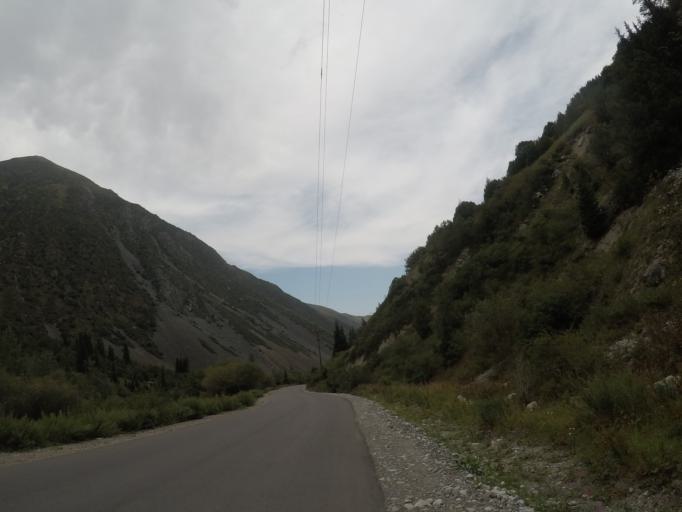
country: KG
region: Chuy
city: Bishkek
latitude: 42.5757
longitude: 74.4823
